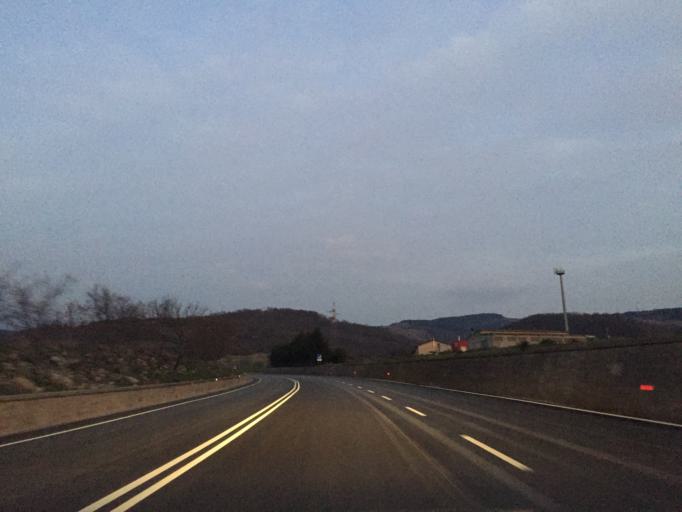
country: IT
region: Apulia
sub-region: Provincia di Foggia
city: Volturino
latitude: 41.4563
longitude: 15.0808
